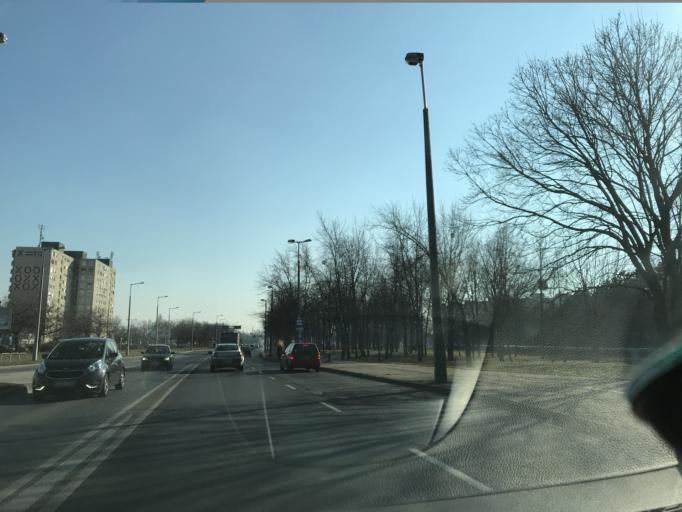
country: HU
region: Gyor-Moson-Sopron
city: Gyor
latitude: 47.6665
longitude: 17.6358
